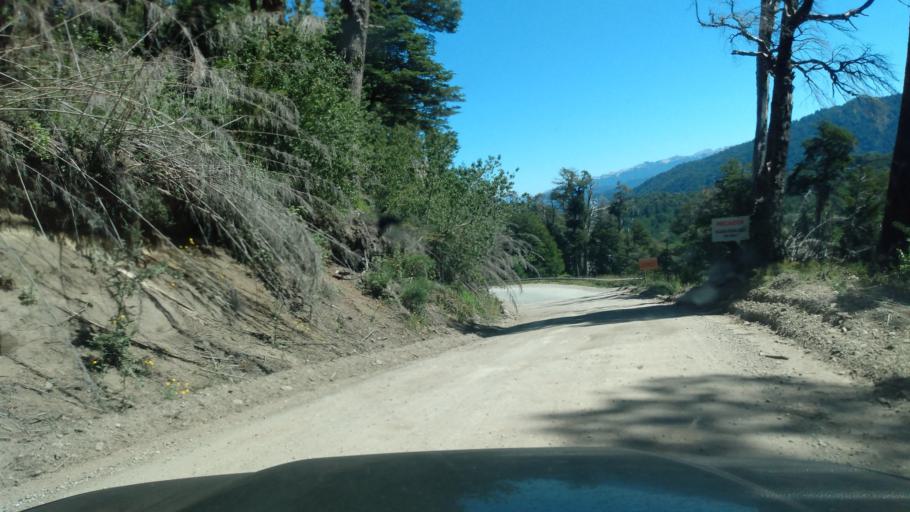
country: AR
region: Neuquen
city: Villa La Angostura
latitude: -40.6099
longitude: -71.6434
